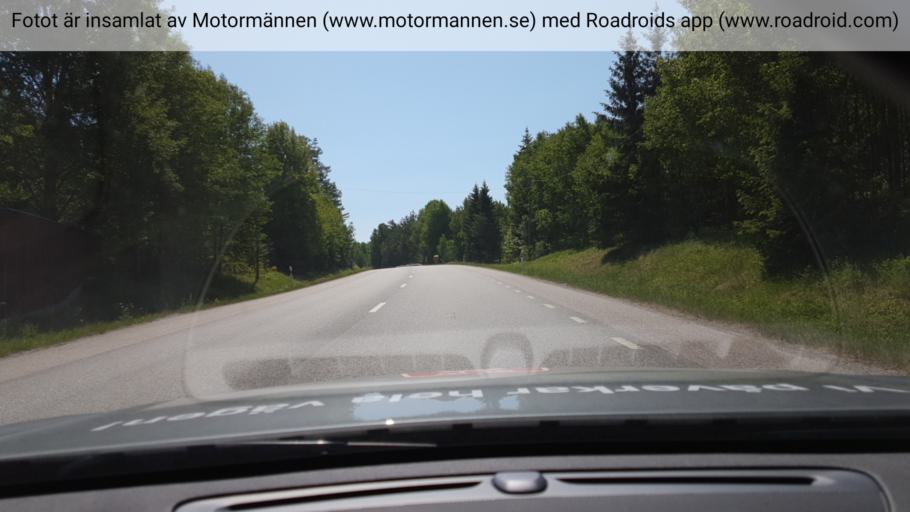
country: SE
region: Stockholm
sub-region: Norrtalje Kommun
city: Rimbo
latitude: 59.6438
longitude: 18.3327
